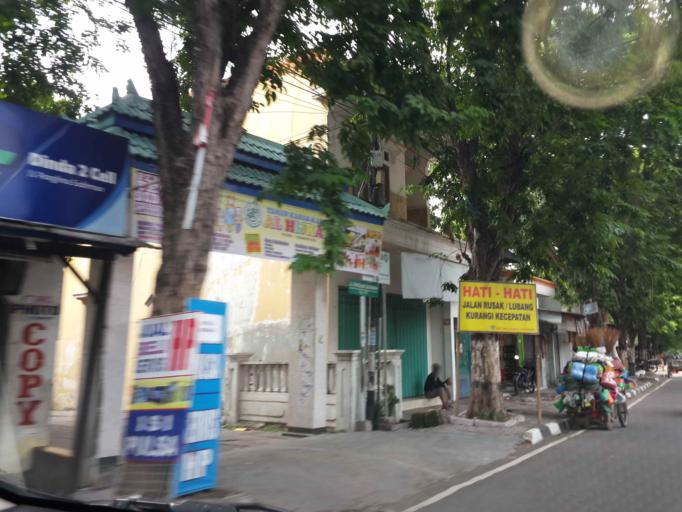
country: ID
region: East Java
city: Gresik
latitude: -7.1700
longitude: 112.6540
